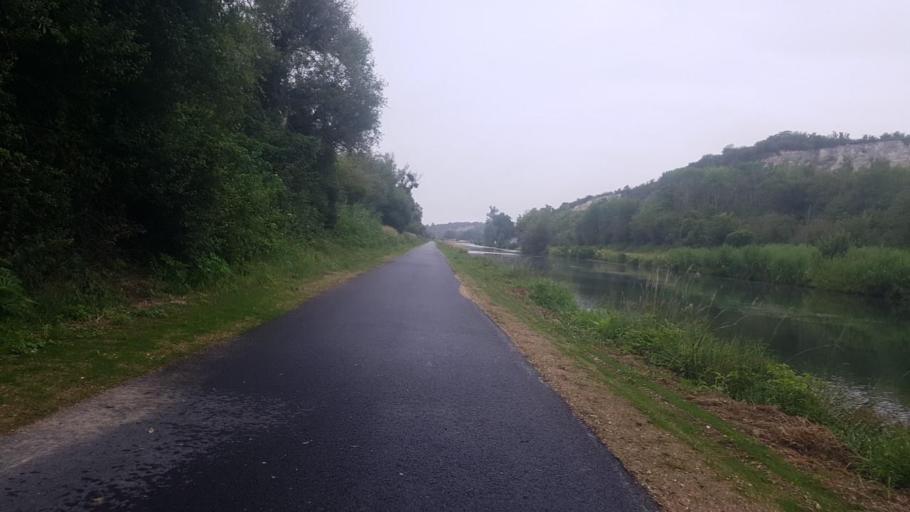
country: FR
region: Champagne-Ardenne
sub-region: Departement de la Marne
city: Vitry-le-Francois
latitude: 48.7834
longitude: 4.5375
